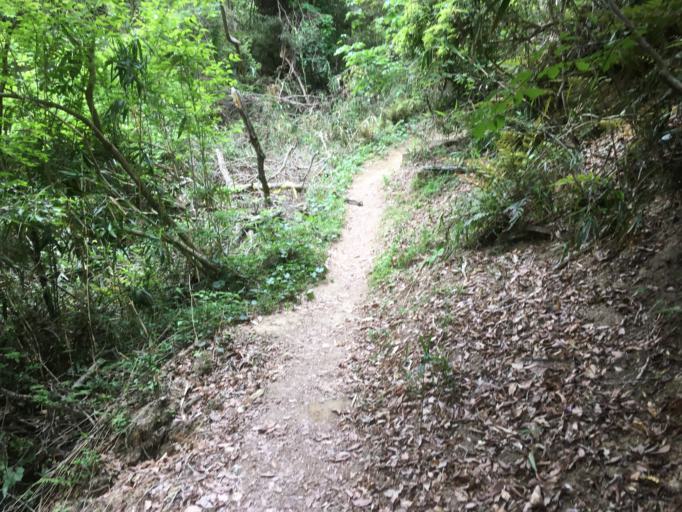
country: JP
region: Nara
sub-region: Ikoma-shi
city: Ikoma
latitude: 34.7010
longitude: 135.6727
